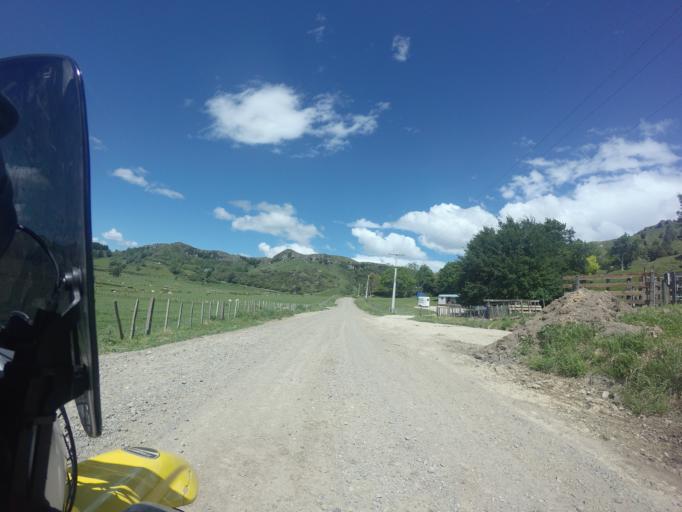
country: NZ
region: Hawke's Bay
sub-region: Wairoa District
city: Wairoa
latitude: -38.9895
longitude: 177.7083
